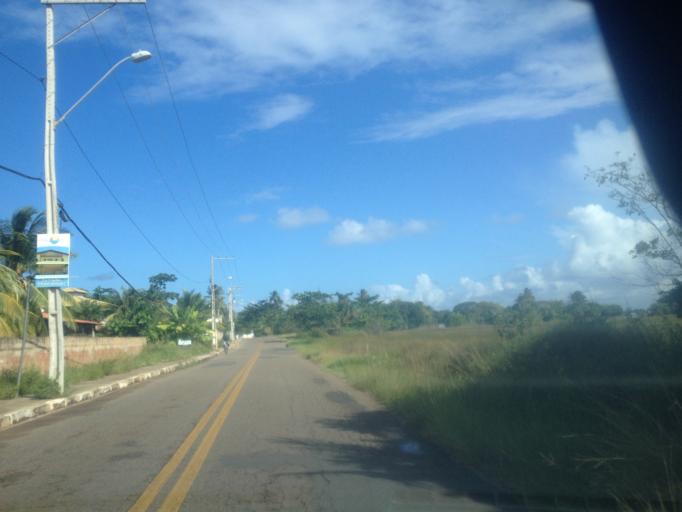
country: BR
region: Bahia
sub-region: Mata De Sao Joao
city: Mata de Sao Joao
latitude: -12.6136
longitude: -38.0440
